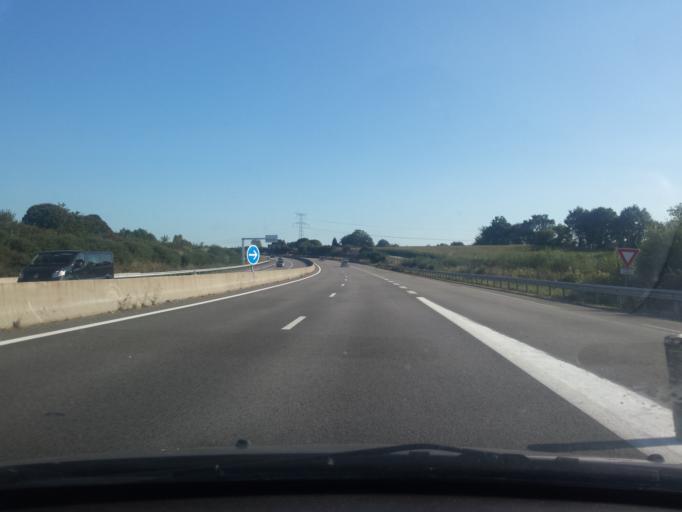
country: FR
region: Brittany
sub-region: Departement du Morbihan
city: Colpo
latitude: 47.7780
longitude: -2.7982
